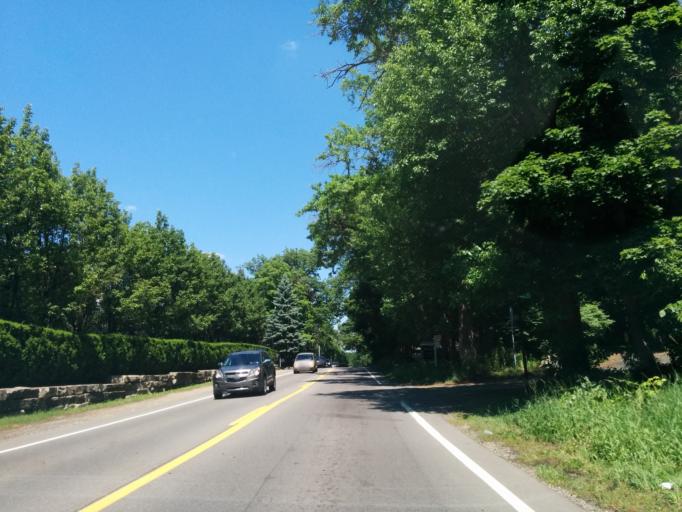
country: US
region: Michigan
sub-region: Oakland County
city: Orchard Lake
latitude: 42.5771
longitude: -83.3666
